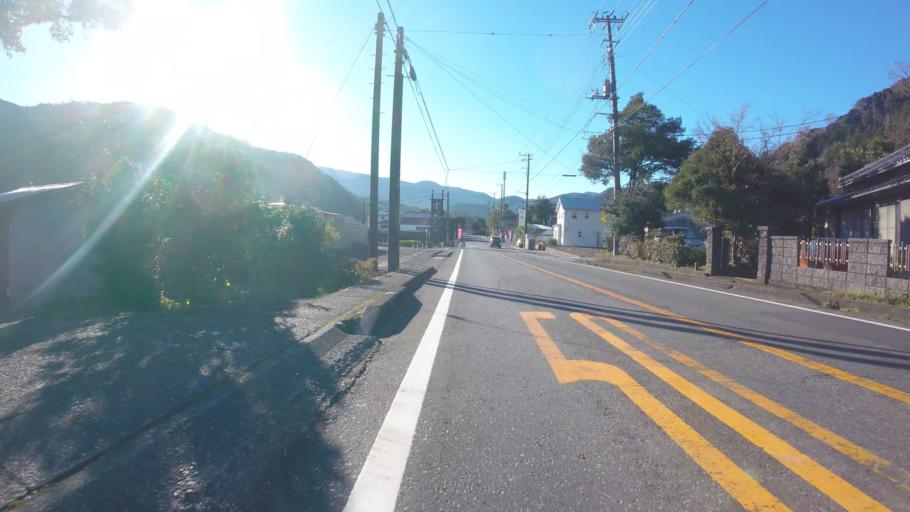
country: JP
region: Shizuoka
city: Heda
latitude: 34.9140
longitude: 138.9241
